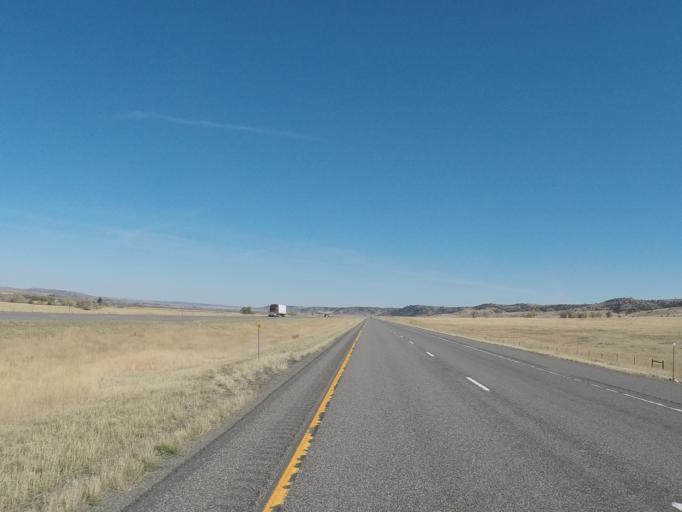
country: US
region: Montana
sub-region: Sweet Grass County
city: Big Timber
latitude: 45.7532
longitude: -110.1478
